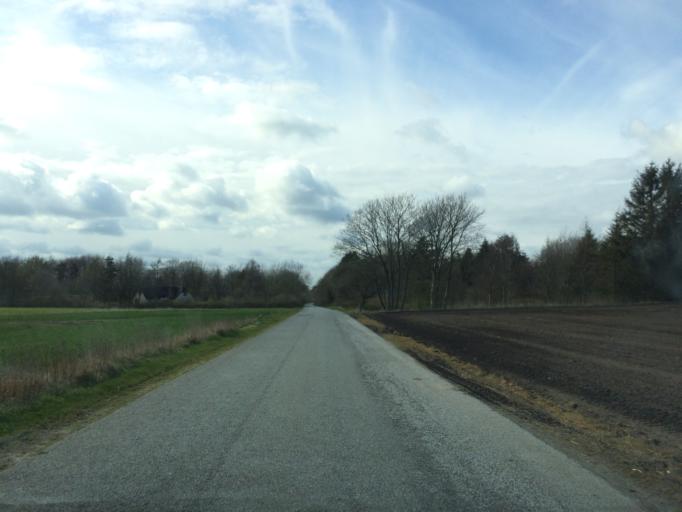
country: DK
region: Central Jutland
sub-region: Ringkobing-Skjern Kommune
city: Videbaek
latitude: 56.2056
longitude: 8.5491
